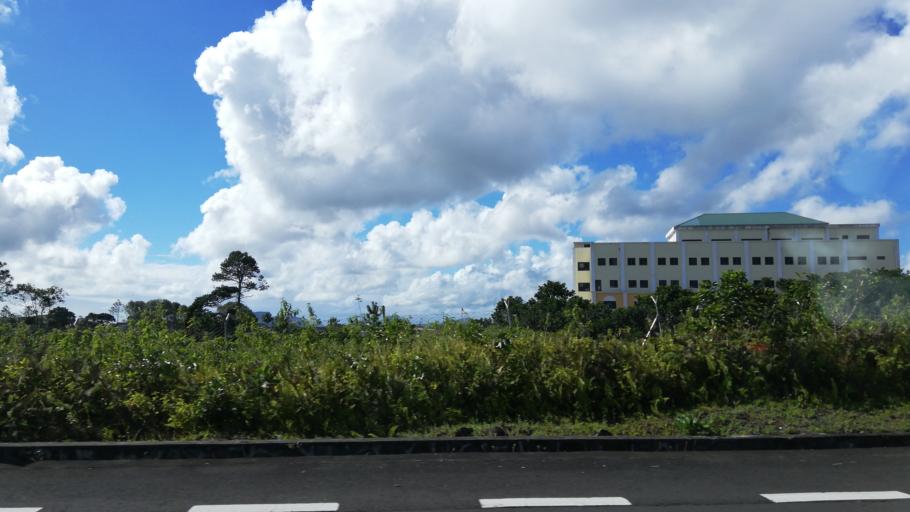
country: MU
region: Moka
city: Quartier Militaire
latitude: -20.2513
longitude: 57.5858
